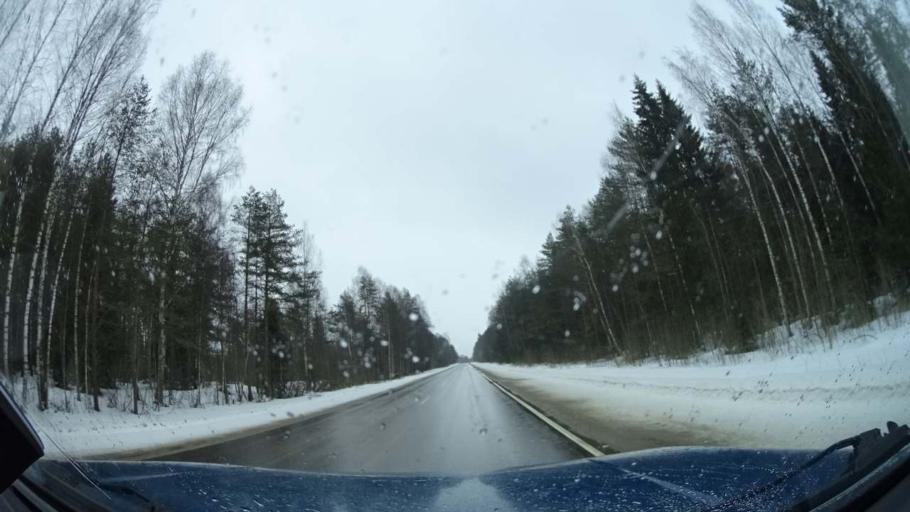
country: RU
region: Tverskaya
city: Radchenko
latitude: 56.8515
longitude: 36.5083
